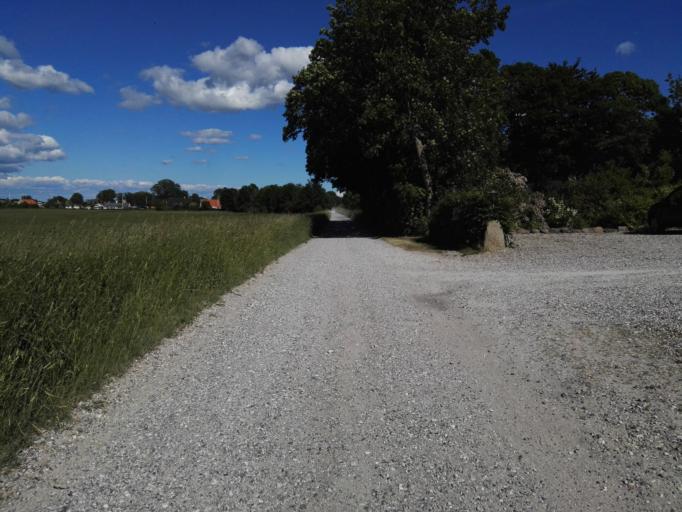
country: DK
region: Capital Region
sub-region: Frederikssund Kommune
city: Frederikssund
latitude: 55.8612
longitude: 12.0888
